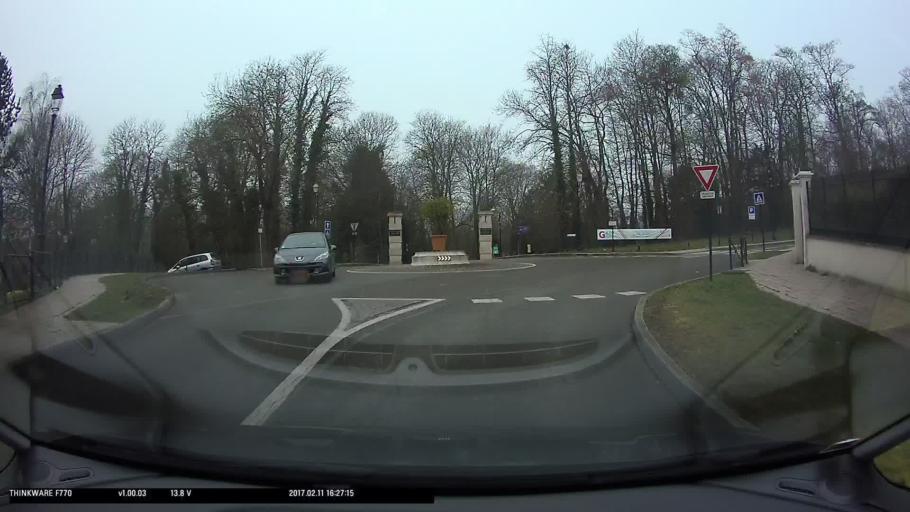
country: FR
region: Ile-de-France
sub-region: Departement du Val-d'Oise
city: Osny
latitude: 49.0633
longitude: 2.0650
